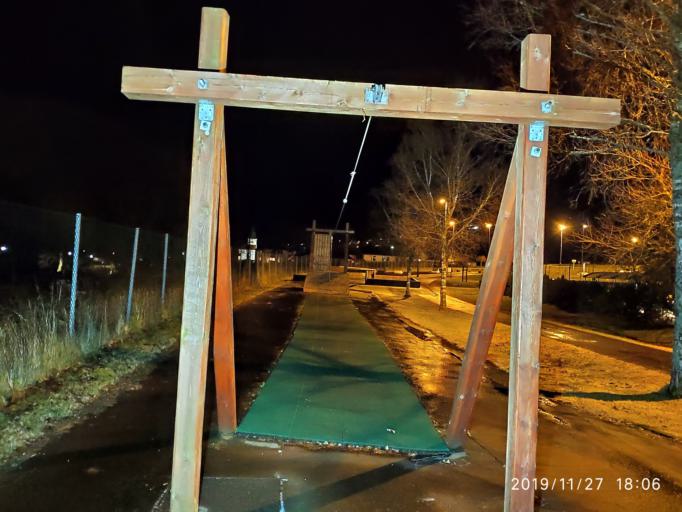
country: NO
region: Rogaland
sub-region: Lund
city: Moi
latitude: 58.4506
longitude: 6.5534
